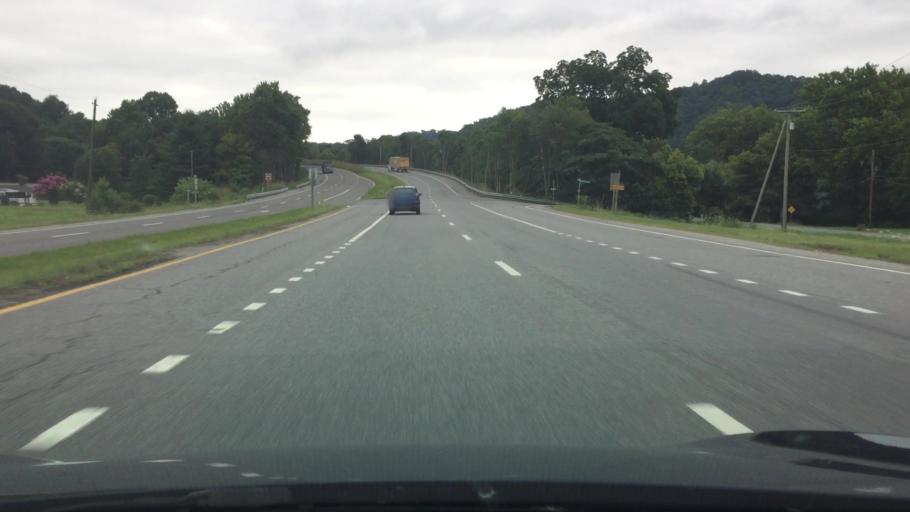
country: US
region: Virginia
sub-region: Montgomery County
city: Shawsville
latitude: 37.2213
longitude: -80.2237
